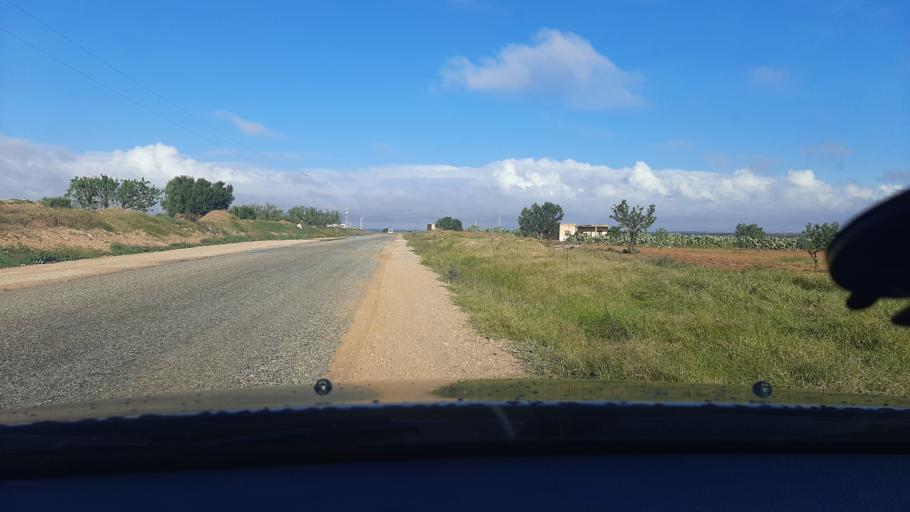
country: TN
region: Safaqis
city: Sfax
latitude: 34.8792
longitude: 10.6339
